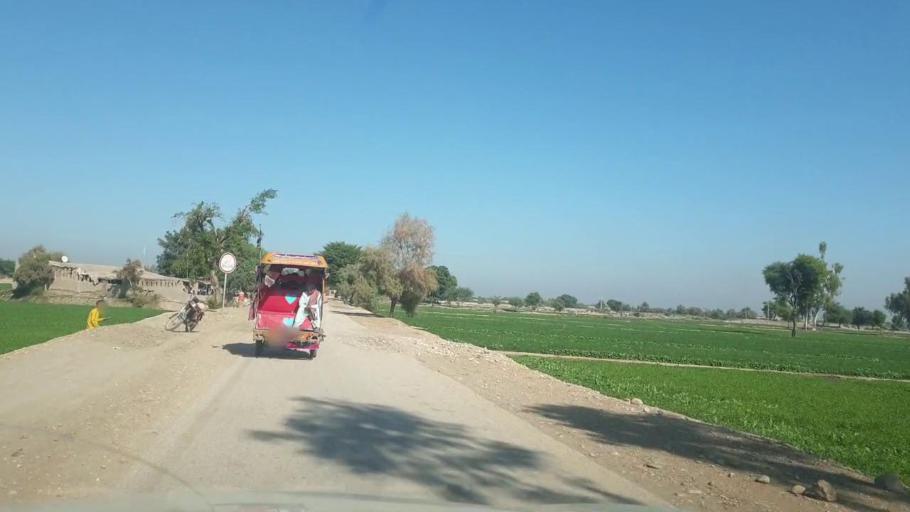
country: PK
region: Sindh
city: Bhan
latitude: 26.5532
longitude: 67.6335
